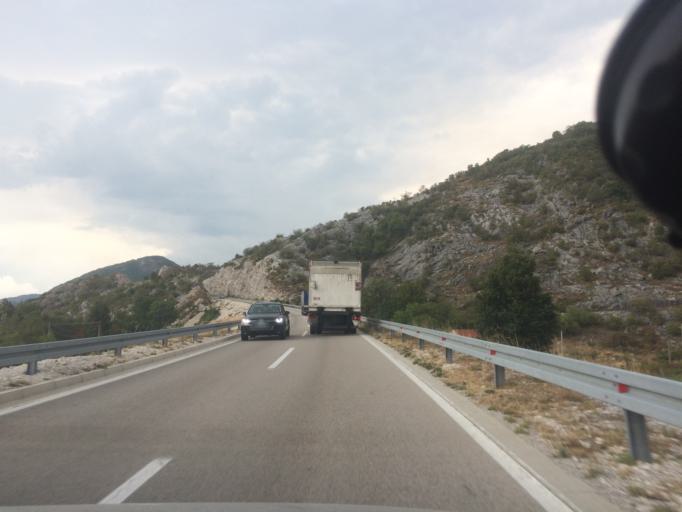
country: ME
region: Kotor
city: Risan
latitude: 42.6540
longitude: 18.6761
